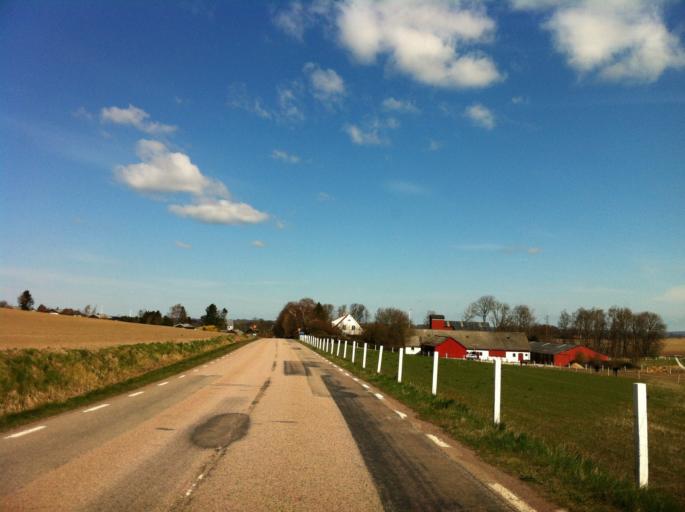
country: SE
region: Skane
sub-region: Landskrona
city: Landskrona
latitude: 55.9166
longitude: 12.8725
